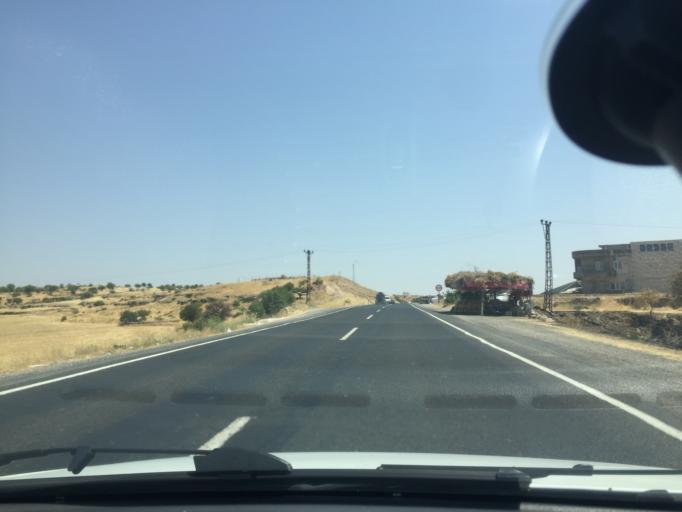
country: TR
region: Mardin
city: Acirli
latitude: 37.4474
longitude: 41.2767
